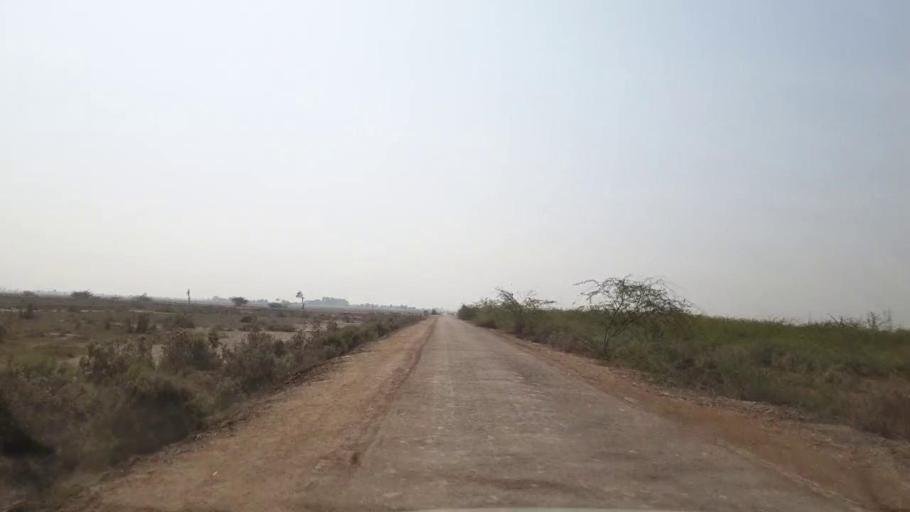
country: PK
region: Sindh
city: Mirpur Khas
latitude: 25.5844
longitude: 69.0254
